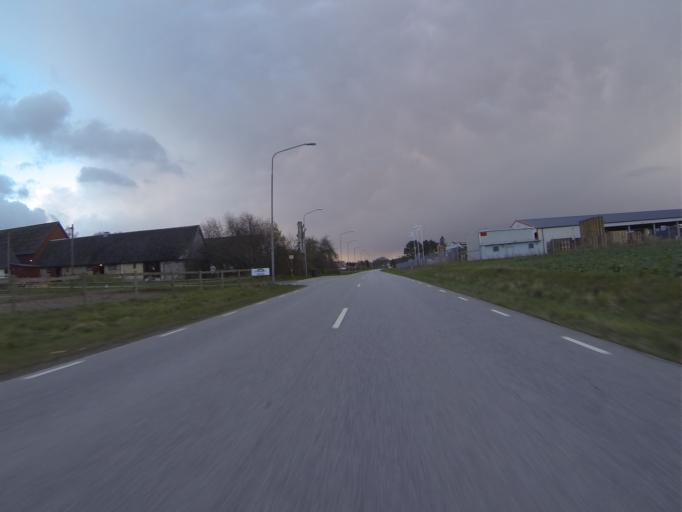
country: SE
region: Skane
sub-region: Lunds Kommun
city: Genarp
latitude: 55.6065
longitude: 13.4039
